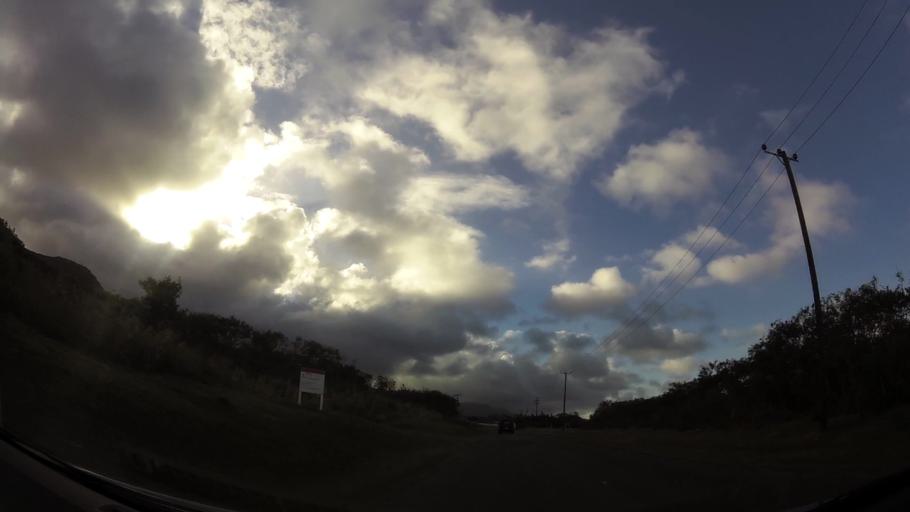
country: KN
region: Saint Mary Cayon
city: Cayon
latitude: 17.3475
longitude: -62.7240
